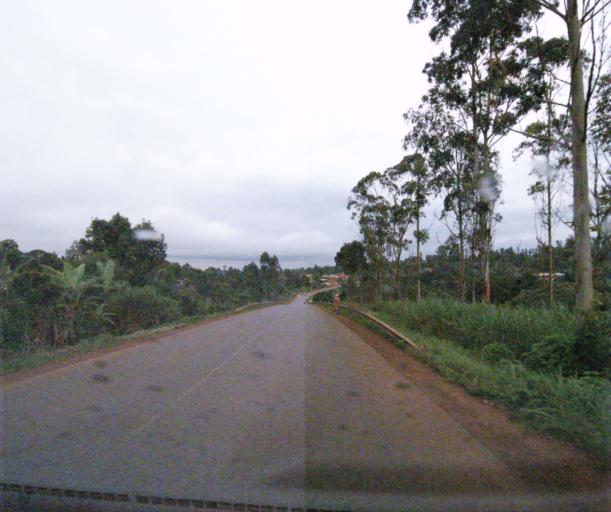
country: CM
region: West
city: Bansoa
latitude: 5.4902
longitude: 10.1839
